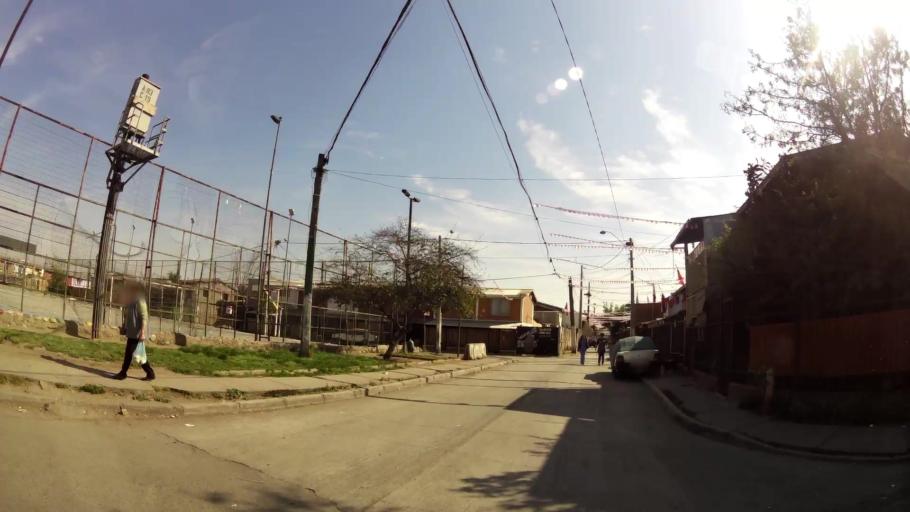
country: CL
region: Santiago Metropolitan
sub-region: Provincia de Santiago
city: La Pintana
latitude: -33.5627
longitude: -70.6390
